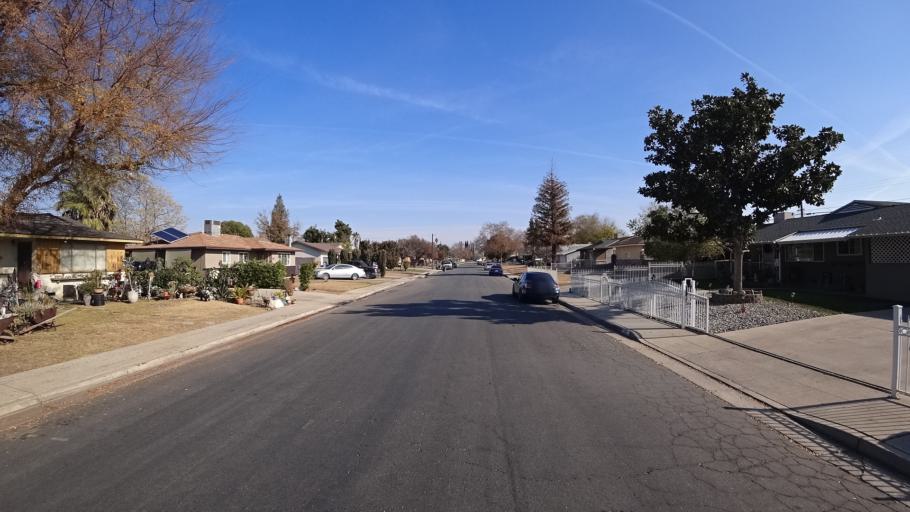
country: US
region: California
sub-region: Kern County
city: Bakersfield
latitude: 35.3289
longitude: -119.0198
